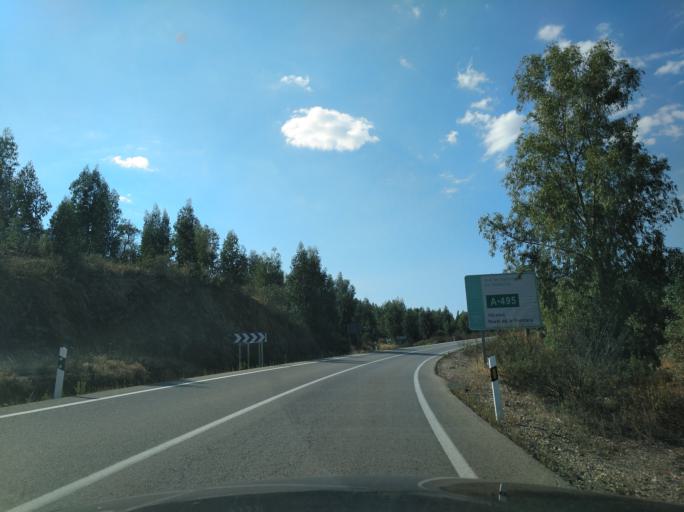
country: ES
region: Andalusia
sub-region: Provincia de Huelva
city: Santa Barbara de Casa
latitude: 37.8044
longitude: -7.2017
